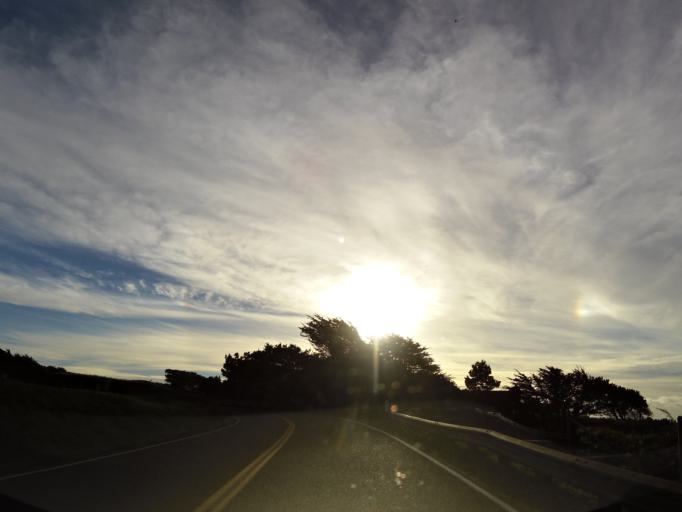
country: US
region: California
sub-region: Mendocino County
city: Fort Bragg
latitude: 39.3146
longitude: -123.8002
